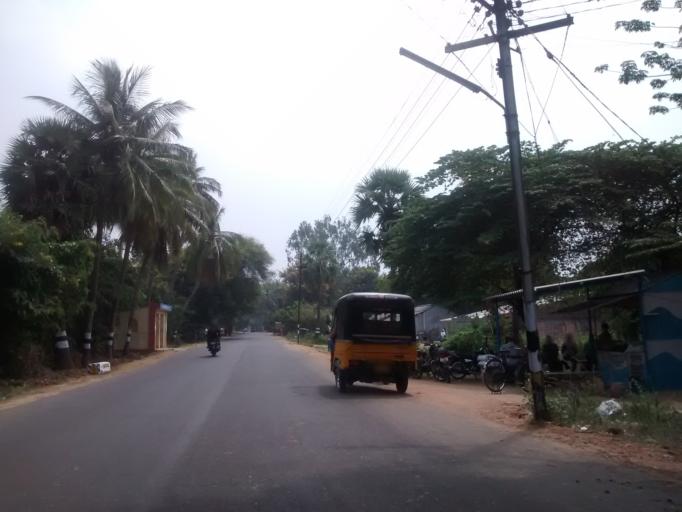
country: IN
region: Tamil Nadu
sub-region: Krishnagiri
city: Krishnagiri
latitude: 12.4745
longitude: 78.1922
